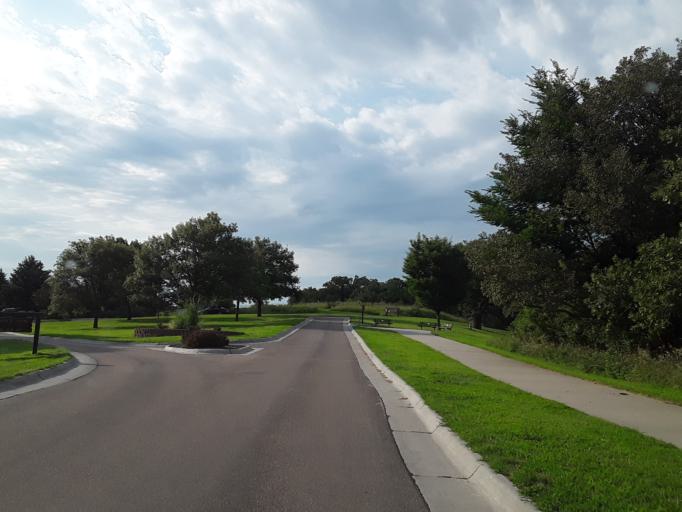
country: US
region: Nebraska
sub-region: Saunders County
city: Ashland
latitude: 41.0320
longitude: -96.3125
